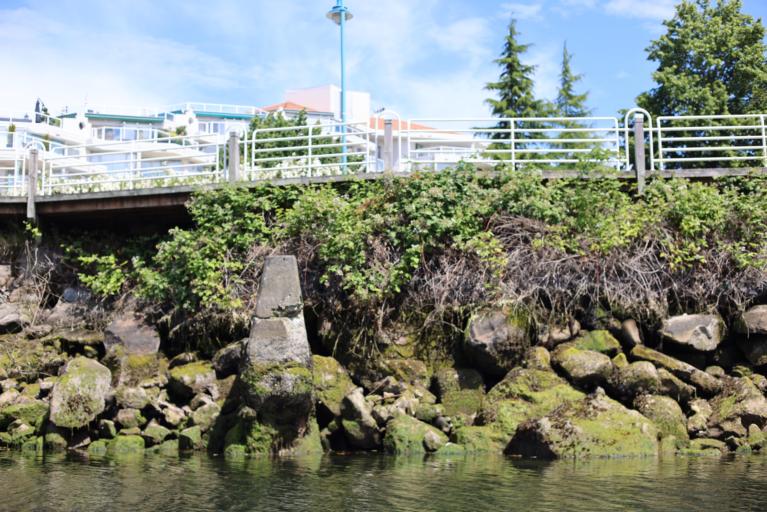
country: CA
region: British Columbia
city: Nanaimo
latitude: 49.1665
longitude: -123.9336
